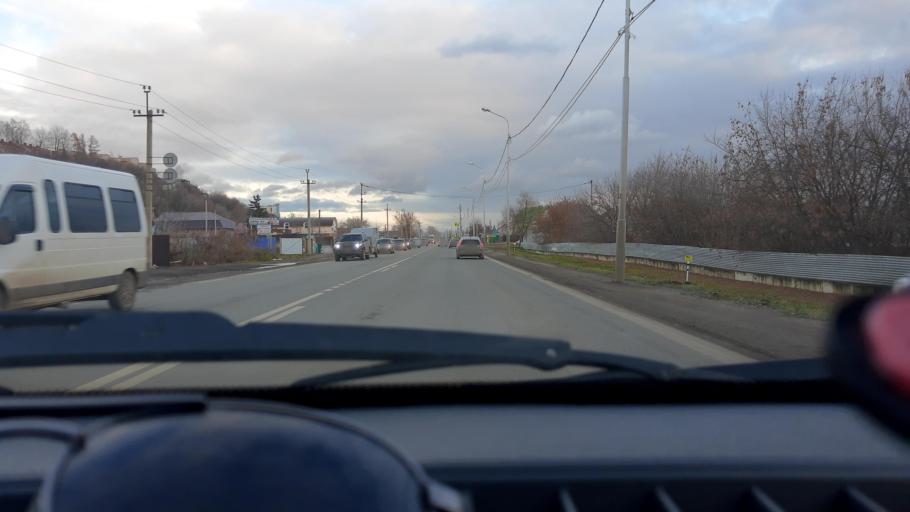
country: RU
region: Bashkortostan
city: Ufa
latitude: 54.6951
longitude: 55.9757
